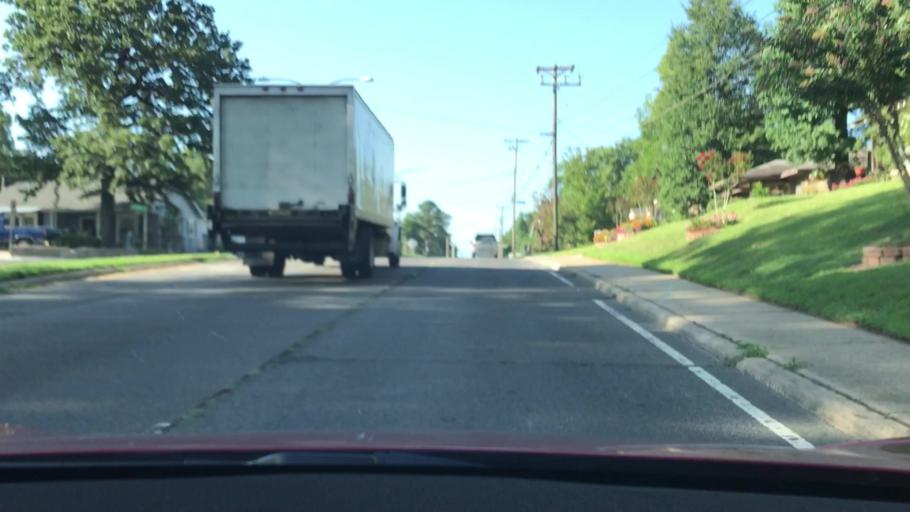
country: US
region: Louisiana
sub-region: Caddo Parish
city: Shreveport
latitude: 32.4685
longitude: -93.7801
